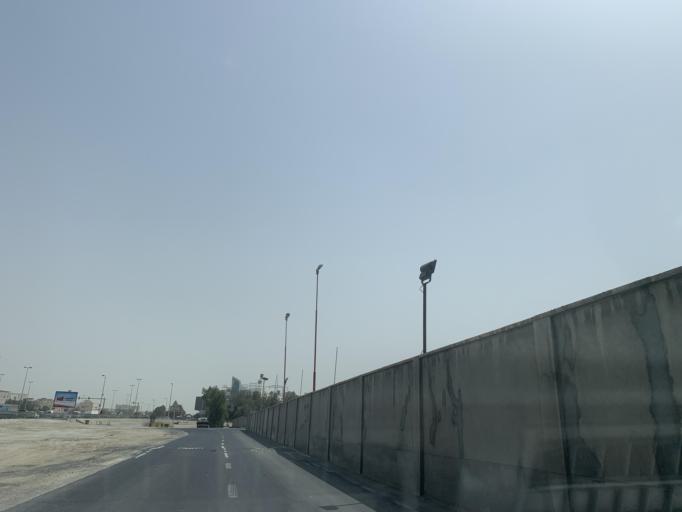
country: BH
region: Northern
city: Madinat `Isa
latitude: 26.1891
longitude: 50.5355
